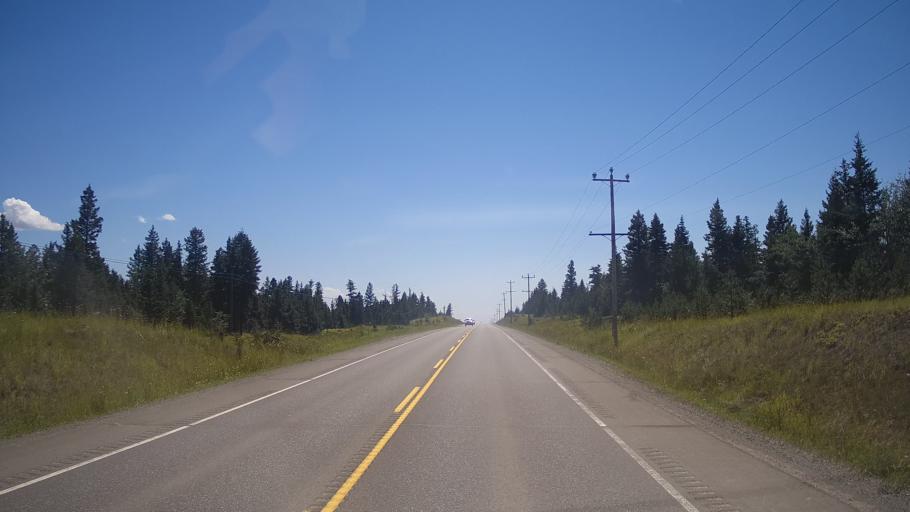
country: CA
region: British Columbia
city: Cache Creek
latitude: 51.1765
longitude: -121.5102
